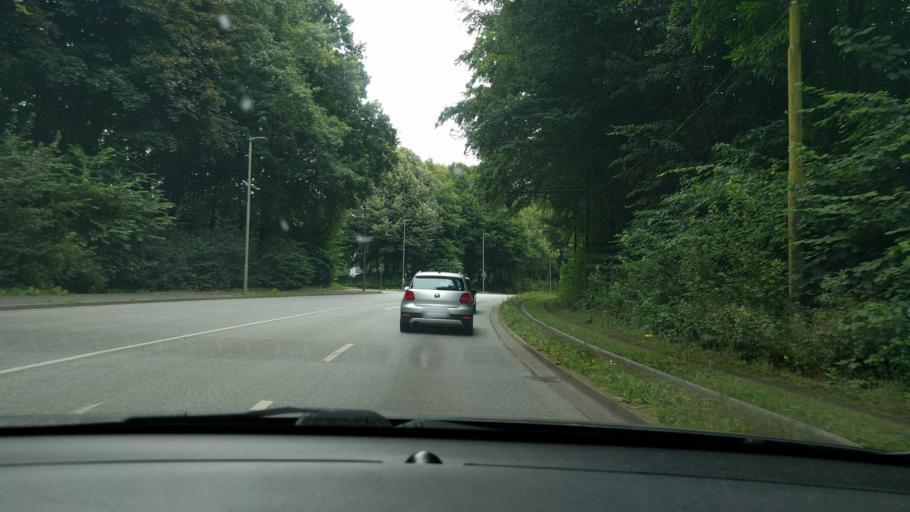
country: DE
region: North Rhine-Westphalia
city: Witten
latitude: 51.4628
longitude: 7.3006
